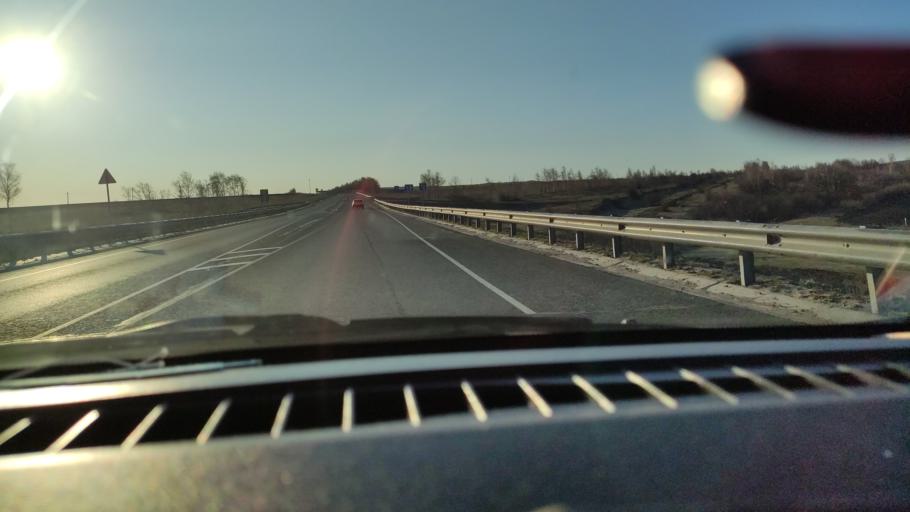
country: RU
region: Saratov
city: Shikhany
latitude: 52.1182
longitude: 47.2764
